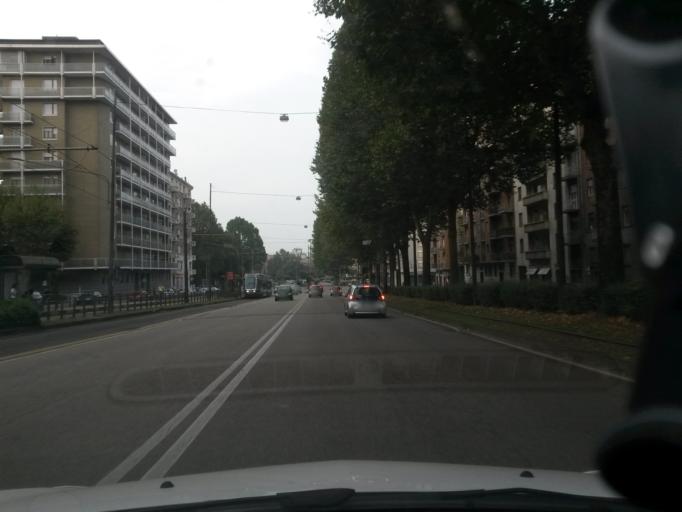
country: IT
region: Piedmont
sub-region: Provincia di Torino
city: Turin
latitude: 45.0845
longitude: 7.6558
